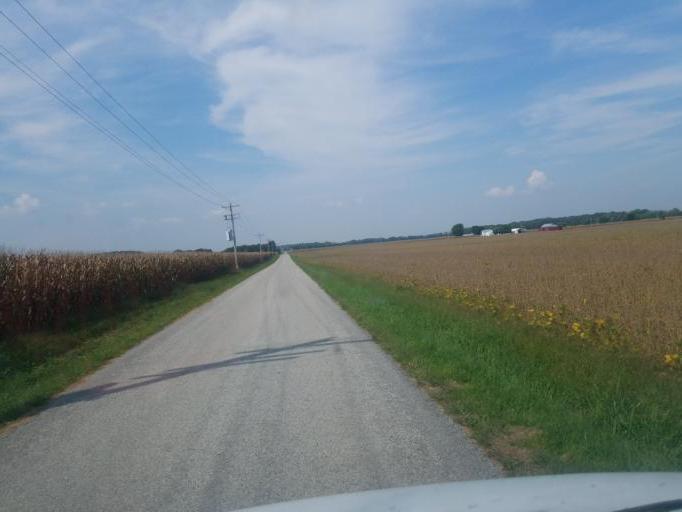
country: US
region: Ohio
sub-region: Wyandot County
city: Upper Sandusky
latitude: 40.6586
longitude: -83.2873
